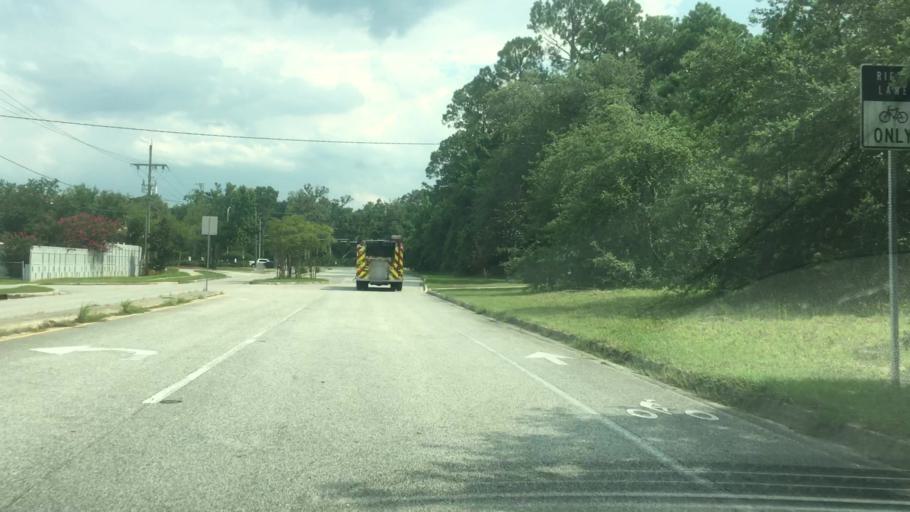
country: US
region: Florida
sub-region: Duval County
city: Neptune Beach
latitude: 30.2891
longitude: -81.5050
